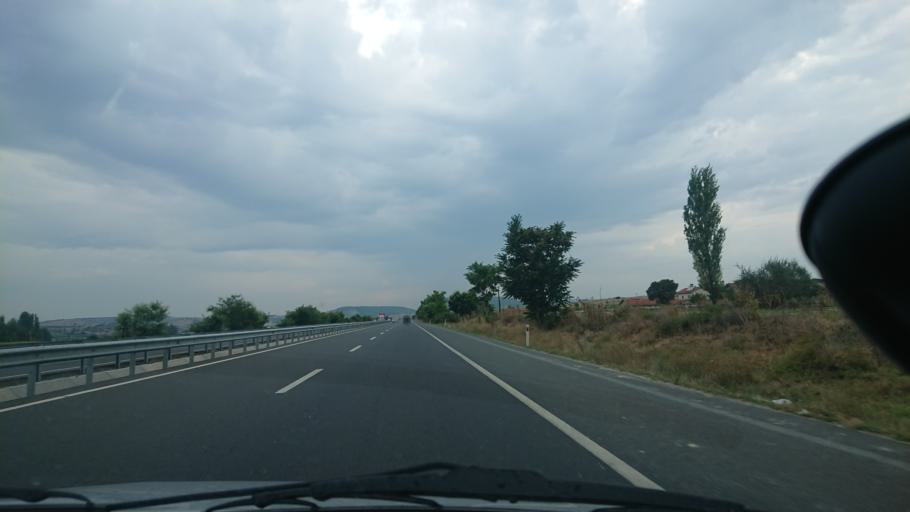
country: TR
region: Manisa
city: Selendi
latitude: 38.6202
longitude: 28.9102
